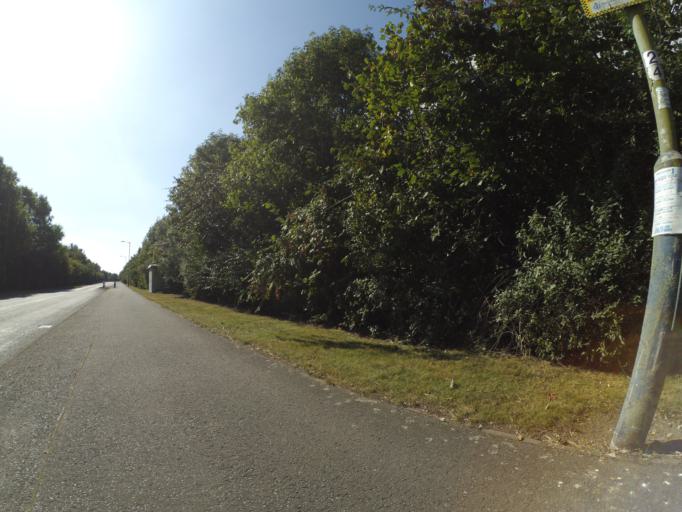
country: GB
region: England
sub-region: Warwickshire
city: Rugby
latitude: 52.3996
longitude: -1.2641
